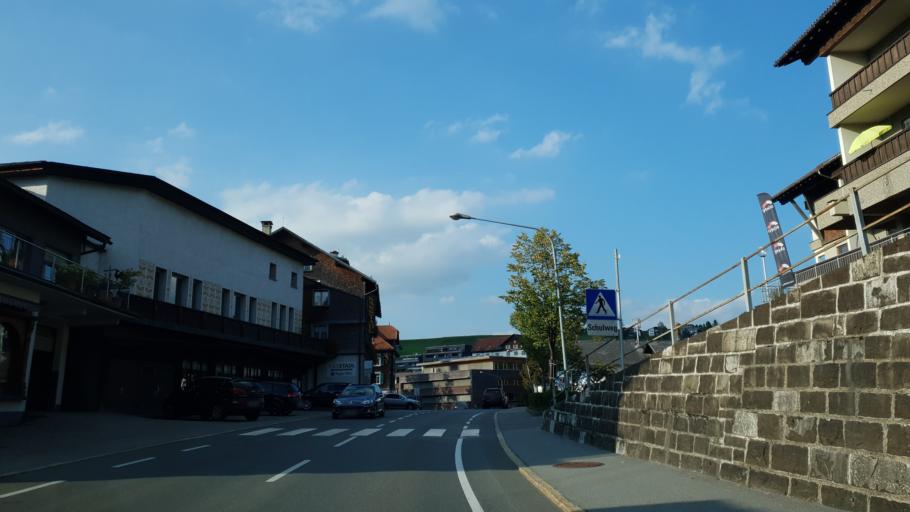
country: AT
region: Vorarlberg
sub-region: Politischer Bezirk Bregenz
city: Egg
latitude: 47.4306
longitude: 9.8971
